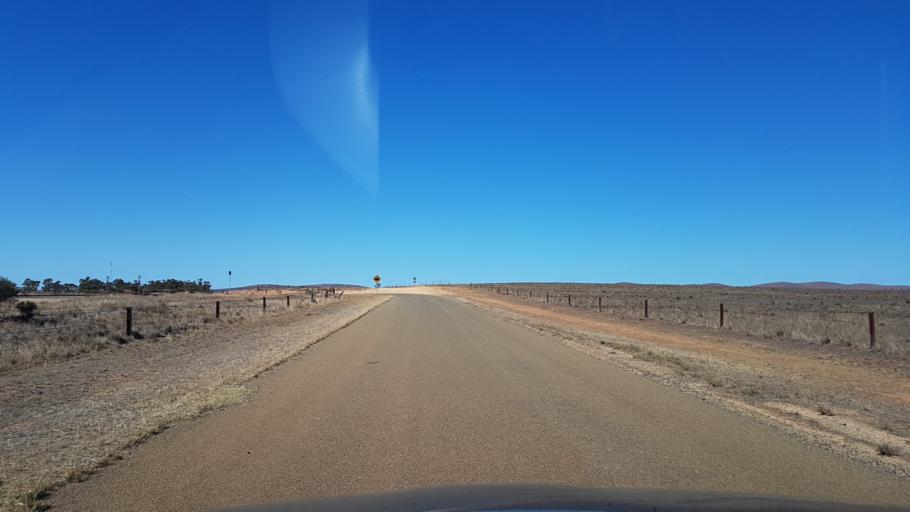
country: AU
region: South Australia
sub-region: Peterborough
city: Peterborough
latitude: -32.9726
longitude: 138.8571
